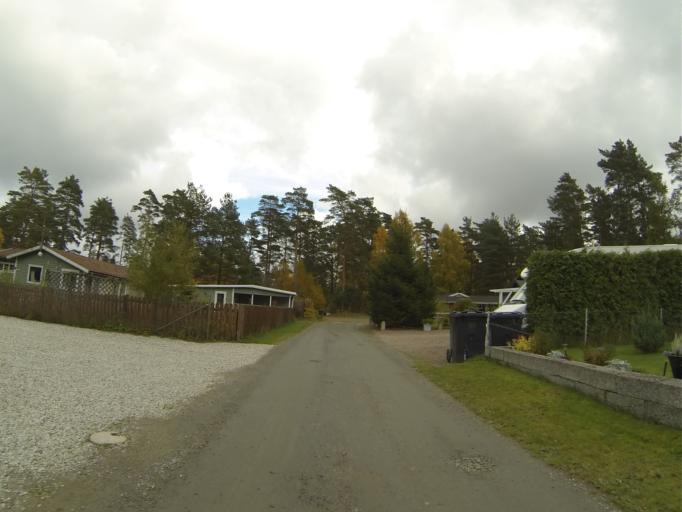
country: SE
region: Skane
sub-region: Sjobo Kommun
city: Sjoebo
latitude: 55.6331
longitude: 13.6497
